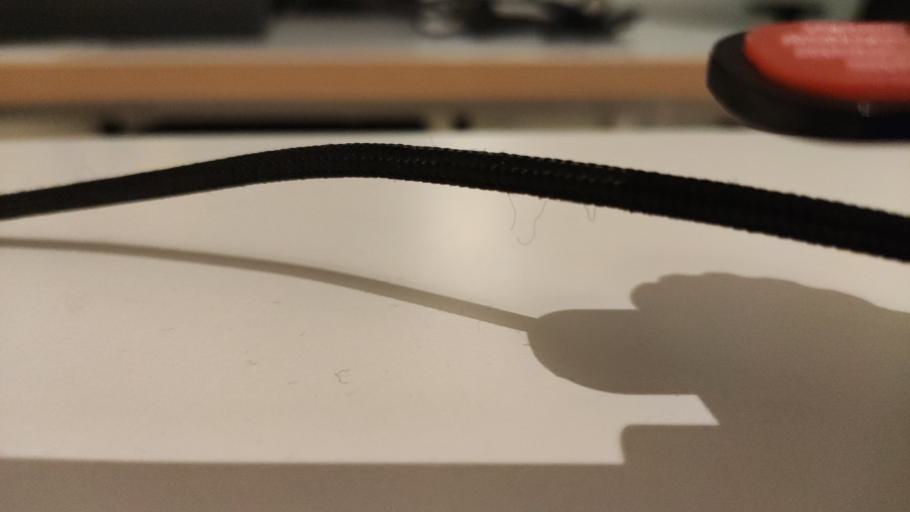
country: RU
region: Moskovskaya
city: Novoye
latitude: 55.6262
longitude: 38.9452
